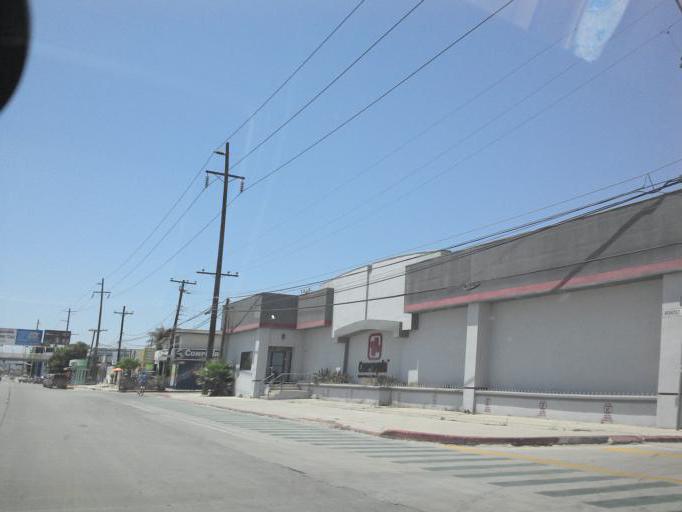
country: MX
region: Baja California
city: Tijuana
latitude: 32.5098
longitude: -116.9777
